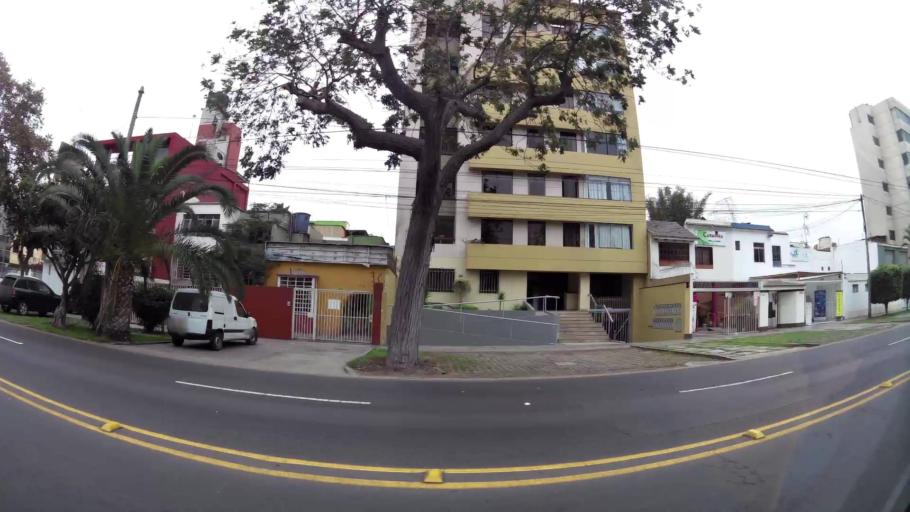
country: PE
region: Lima
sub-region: Lima
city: Surco
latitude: -12.1240
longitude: -77.0182
